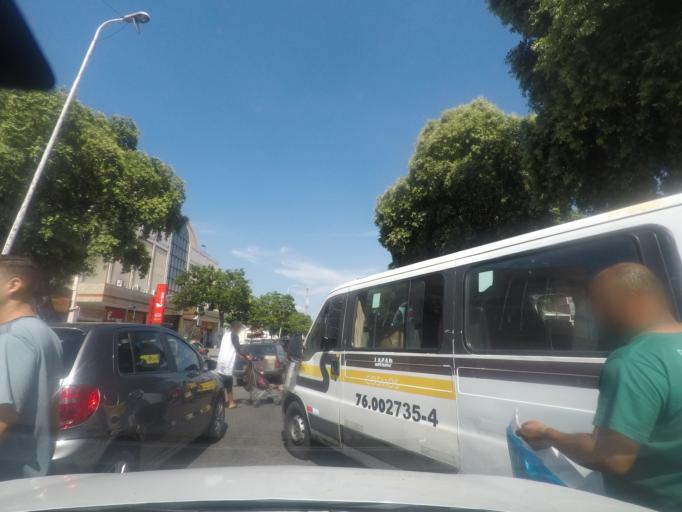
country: BR
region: Rio de Janeiro
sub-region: Nilopolis
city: Nilopolis
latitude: -22.8797
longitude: -43.4646
